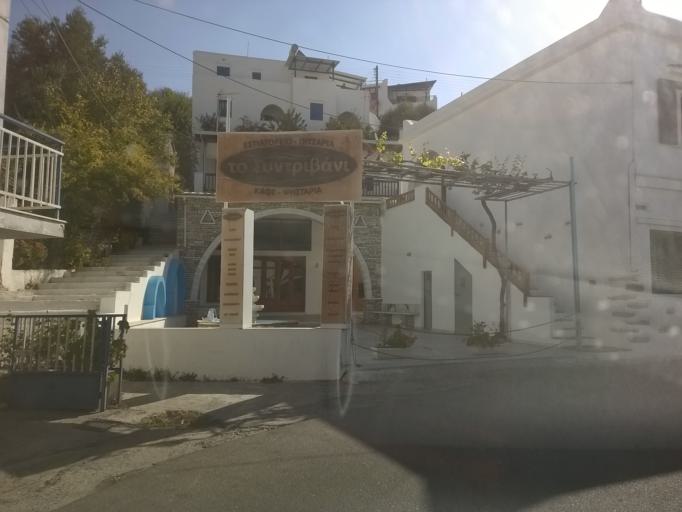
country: GR
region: South Aegean
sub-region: Nomos Kykladon
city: Filotion
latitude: 37.1013
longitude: 25.4801
